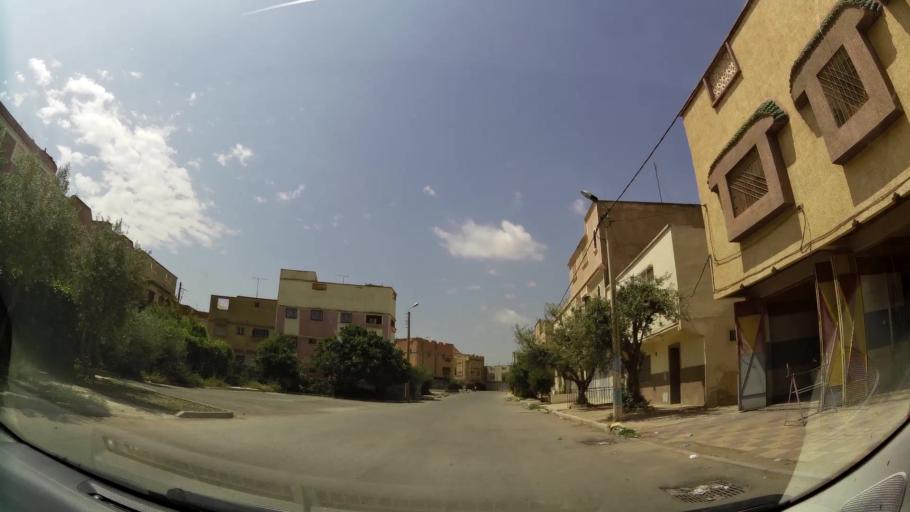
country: MA
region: Oriental
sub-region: Oujda-Angad
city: Oujda
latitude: 34.6844
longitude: -1.8850
